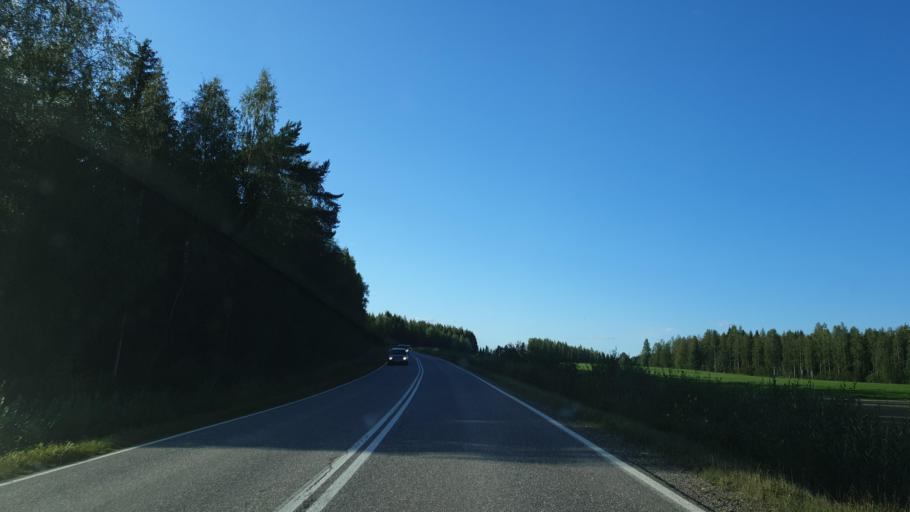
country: FI
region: Northern Savo
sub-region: Koillis-Savo
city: Kaavi
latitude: 62.9843
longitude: 28.4499
